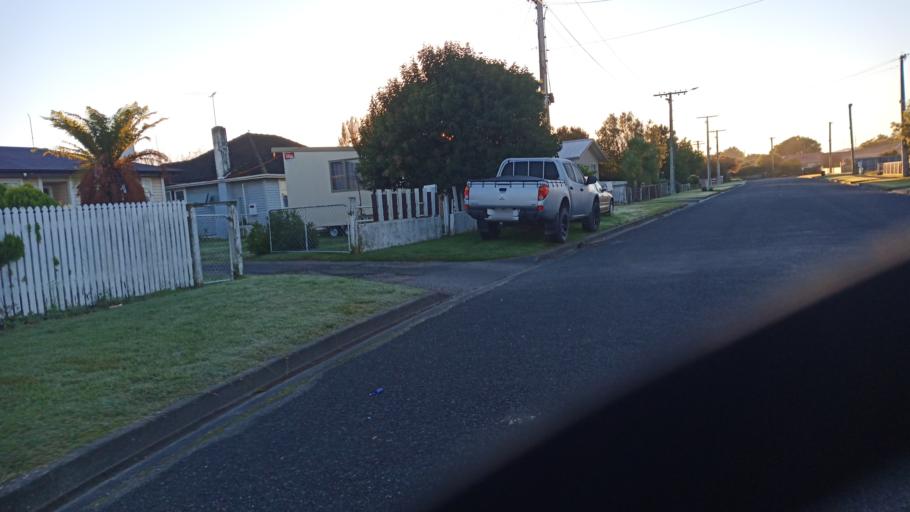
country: NZ
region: Gisborne
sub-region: Gisborne District
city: Gisborne
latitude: -38.6603
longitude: 177.9908
